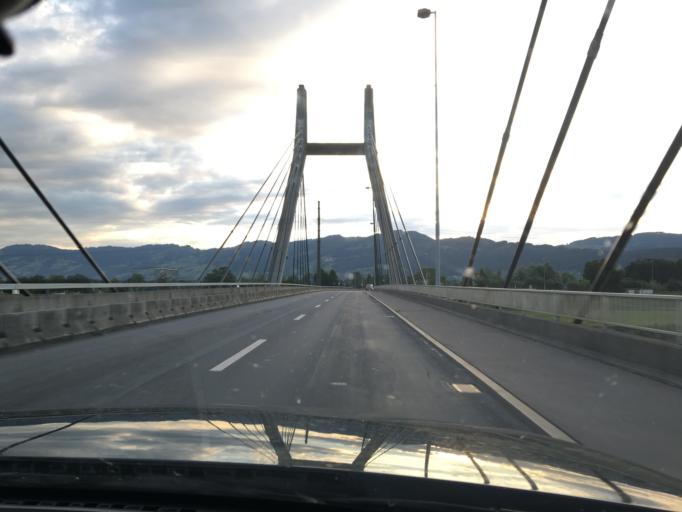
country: CH
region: Saint Gallen
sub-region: Wahlkreis Rheintal
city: Diepoldsau
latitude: 47.3904
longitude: 9.6470
